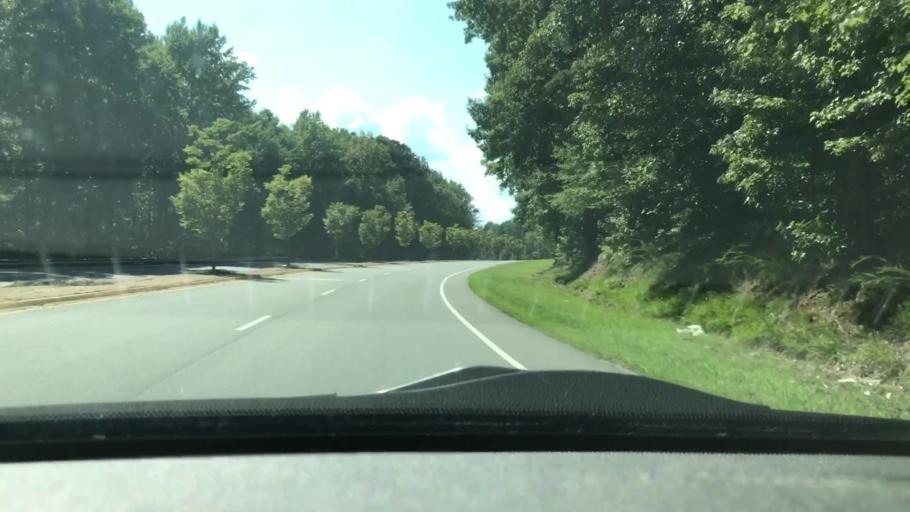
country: US
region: North Carolina
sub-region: Randolph County
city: Asheboro
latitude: 35.7354
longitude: -79.8127
